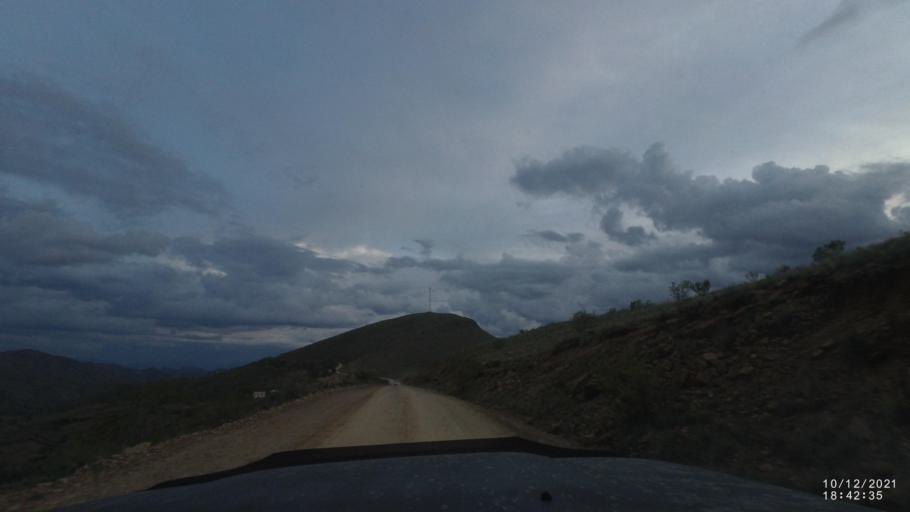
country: BO
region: Cochabamba
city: Tarata
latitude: -17.8708
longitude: -65.9840
